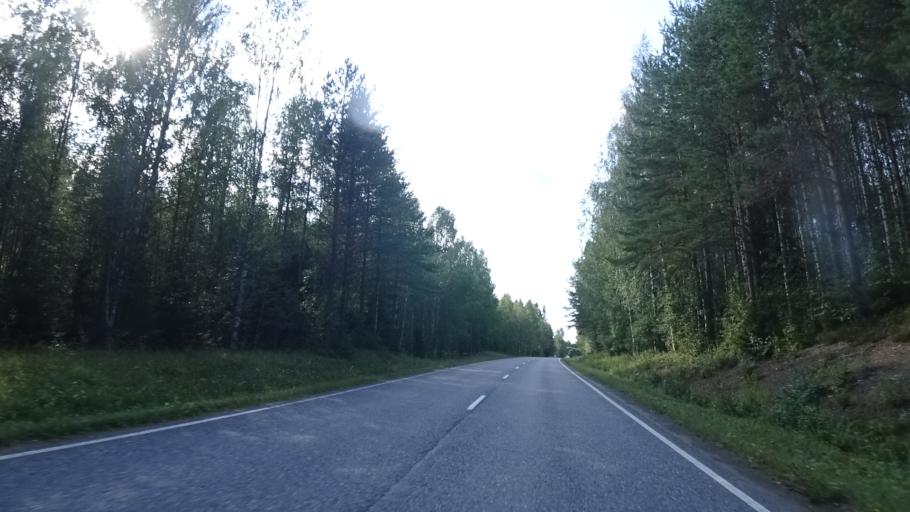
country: FI
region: North Karelia
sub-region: Keski-Karjala
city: Kitee
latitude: 62.0893
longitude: 30.1270
